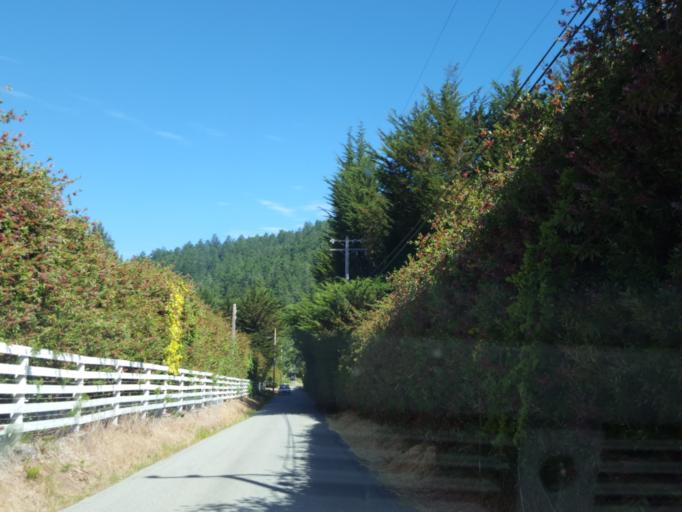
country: US
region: California
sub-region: San Mateo County
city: Portola Valley
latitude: 37.2603
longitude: -122.3240
